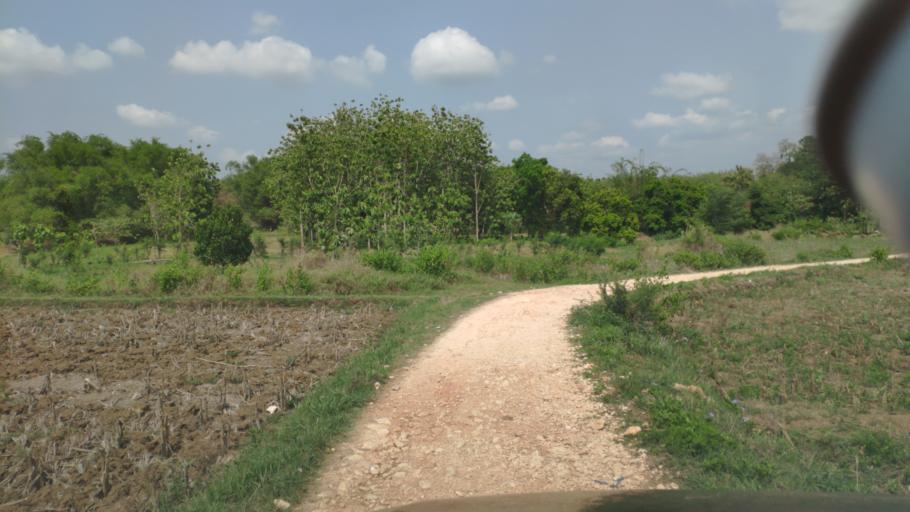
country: ID
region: Central Java
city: Karangboyo
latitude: -7.0914
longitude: 111.5516
